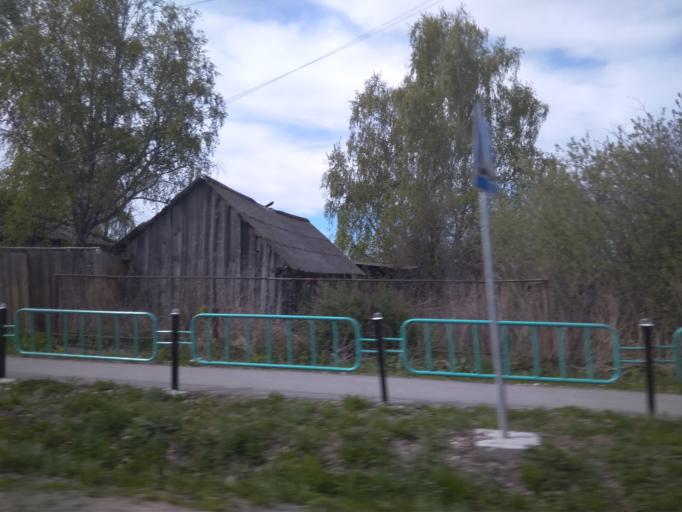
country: RU
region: Mordoviya
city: Chamzinka
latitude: 54.3513
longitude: 45.6723
